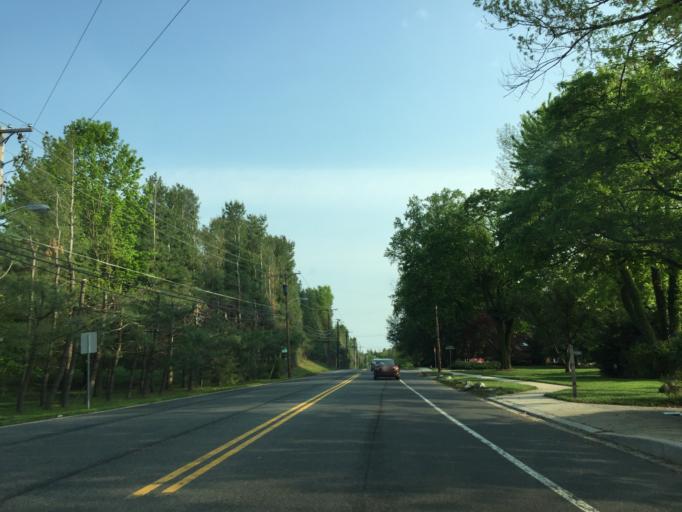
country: US
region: Maryland
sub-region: Baltimore County
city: Pikesville
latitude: 39.3731
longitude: -76.7119
